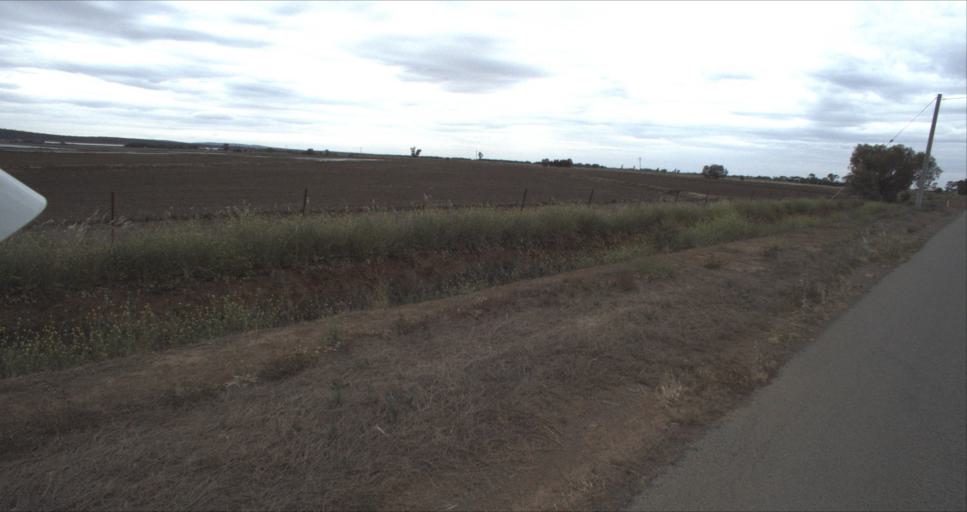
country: AU
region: New South Wales
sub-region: Leeton
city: Leeton
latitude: -34.4140
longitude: 146.3398
